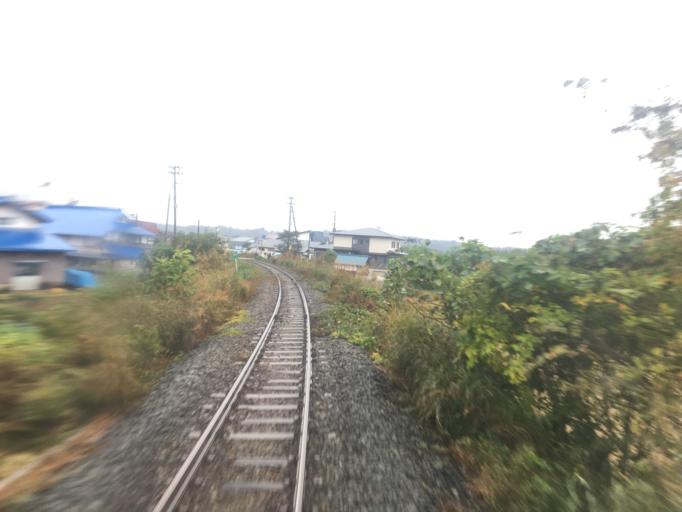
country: JP
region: Yamagata
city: Shinjo
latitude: 38.7058
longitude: 140.3157
